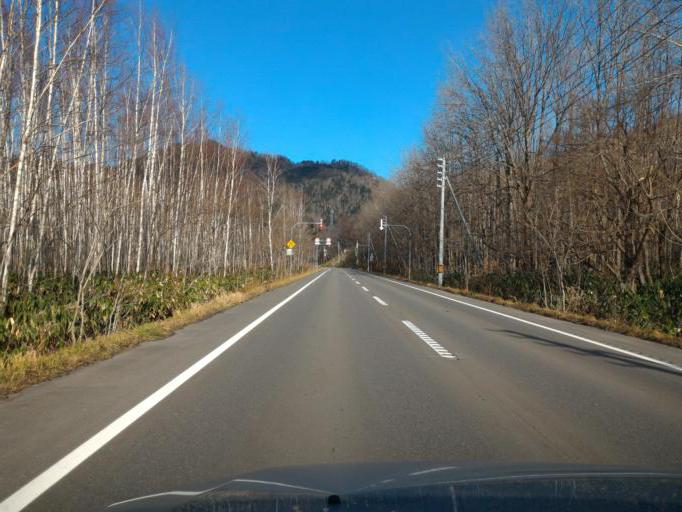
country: JP
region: Hokkaido
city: Ashibetsu
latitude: 43.3641
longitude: 142.1635
